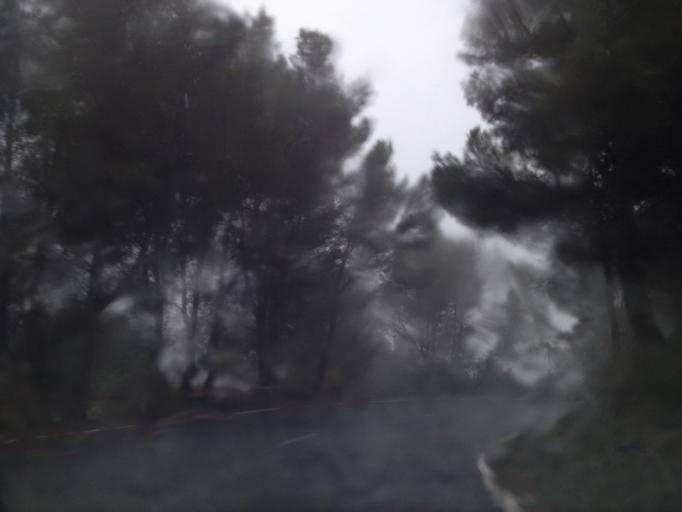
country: ES
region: Balearic Islands
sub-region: Illes Balears
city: Fornalutx
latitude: 39.7906
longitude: 2.7323
